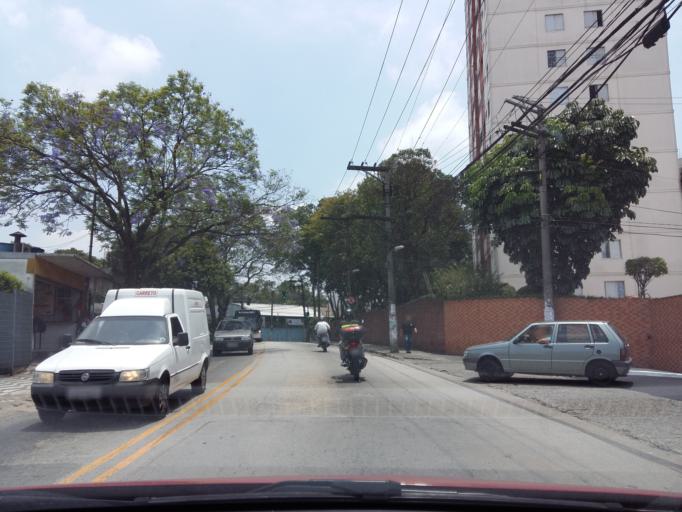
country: BR
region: Sao Paulo
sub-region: Sao Caetano Do Sul
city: Sao Caetano do Sul
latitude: -23.6315
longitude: -46.6044
